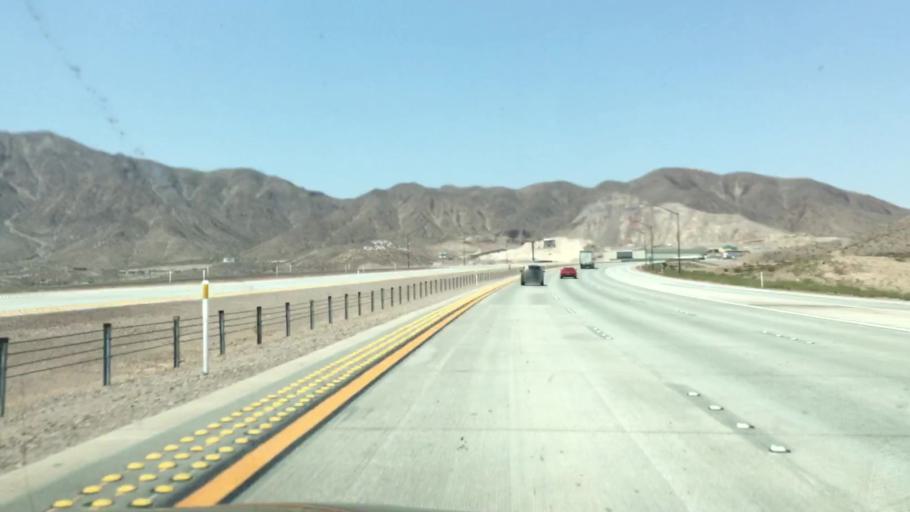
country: US
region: Nevada
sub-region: Clark County
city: Boulder City
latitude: 35.9542
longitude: -114.9054
